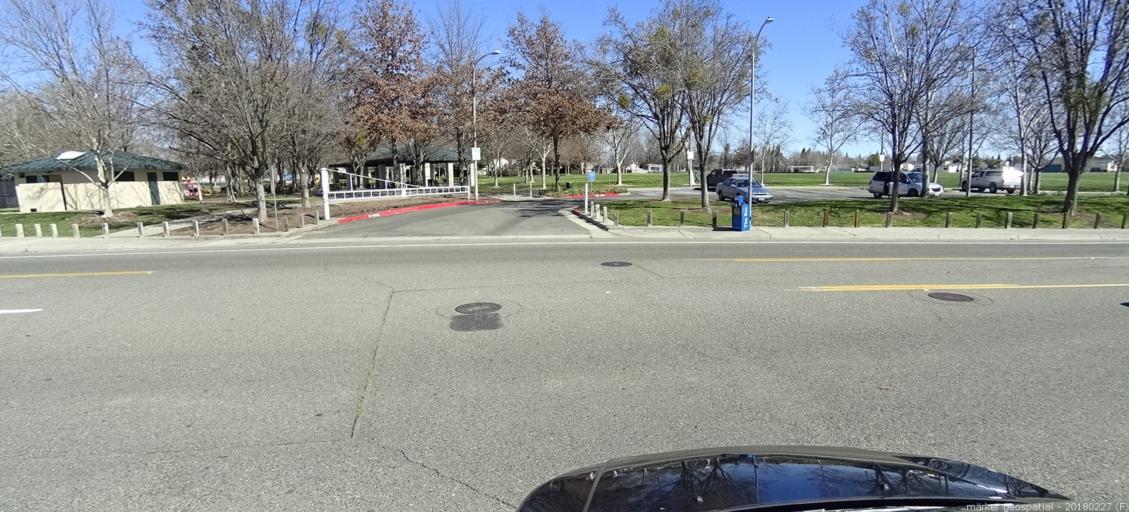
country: US
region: California
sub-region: Sacramento County
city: Antelope
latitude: 38.7180
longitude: -121.3455
